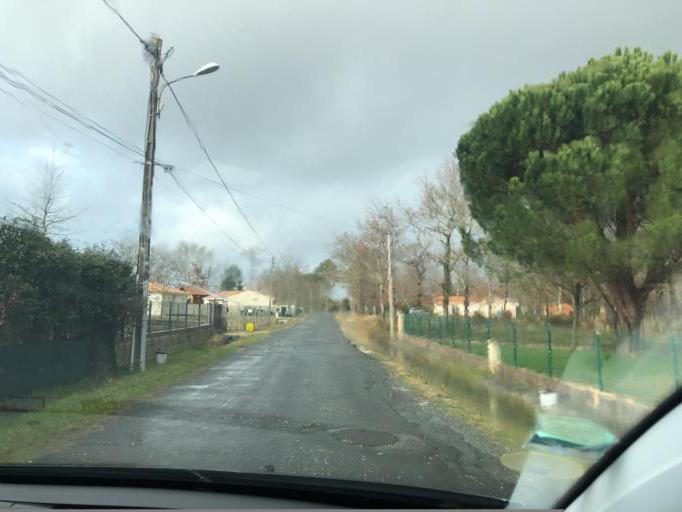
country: FR
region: Aquitaine
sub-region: Departement de la Gironde
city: Hourtin
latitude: 45.1797
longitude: -1.0529
